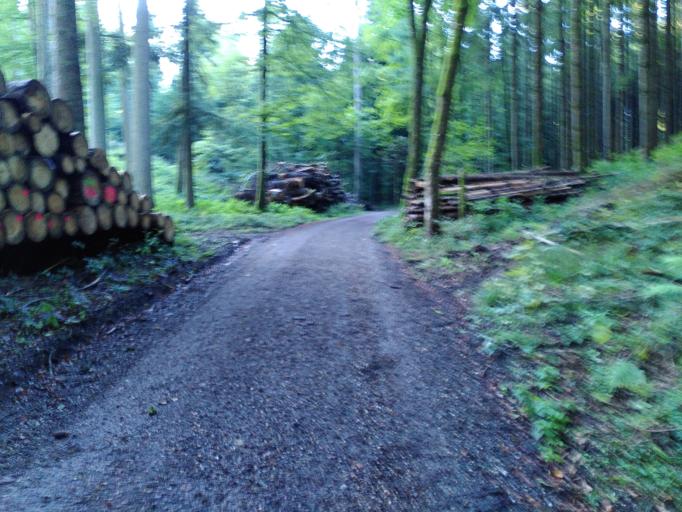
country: CH
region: Bern
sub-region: Emmental District
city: Ersigen
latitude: 47.0989
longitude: 7.6163
